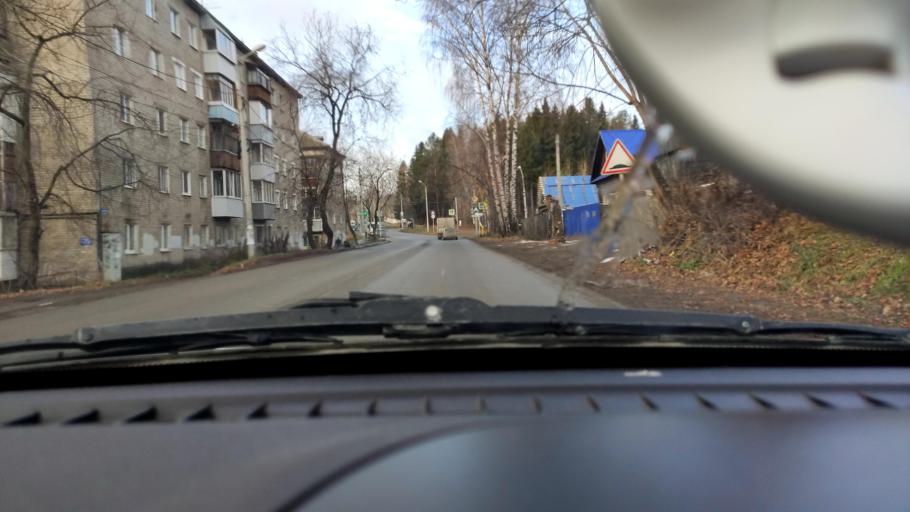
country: RU
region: Perm
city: Kondratovo
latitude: 58.0437
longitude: 56.1023
